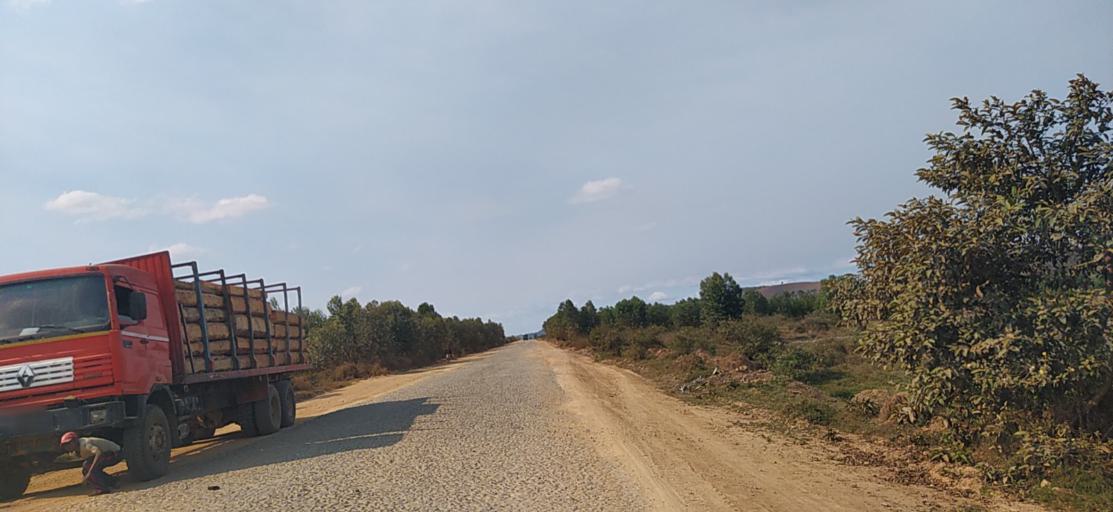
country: MG
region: Alaotra Mangoro
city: Moramanga
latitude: -18.6831
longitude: 48.2718
